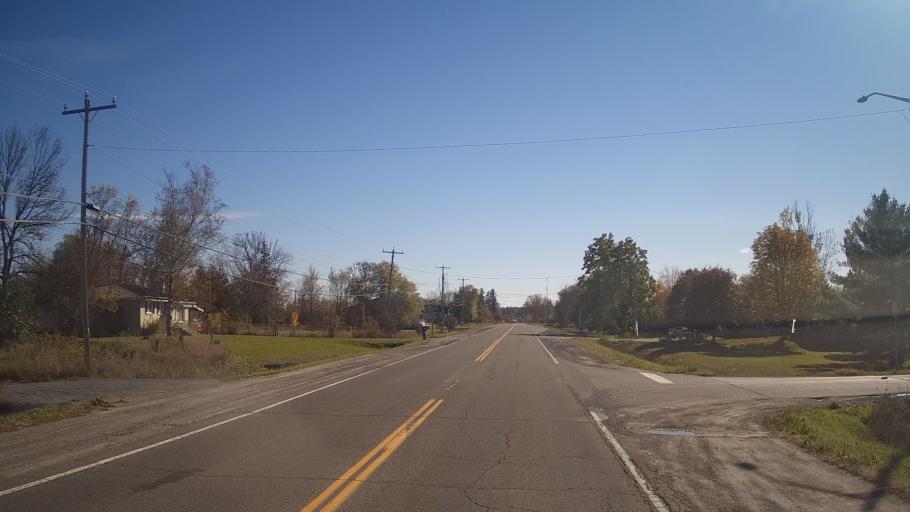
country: CA
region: Ontario
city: Kingston
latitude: 44.4126
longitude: -76.6663
